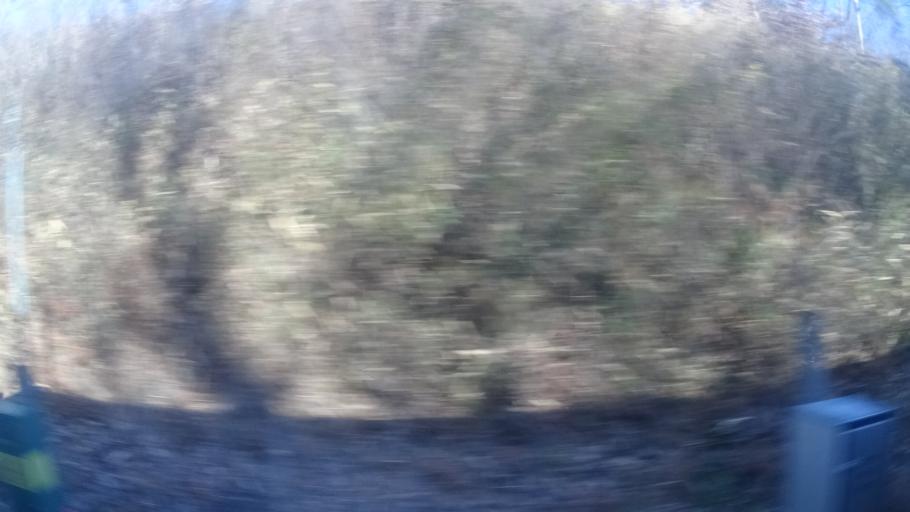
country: JP
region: Miyagi
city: Marumori
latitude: 37.7497
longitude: 140.9389
